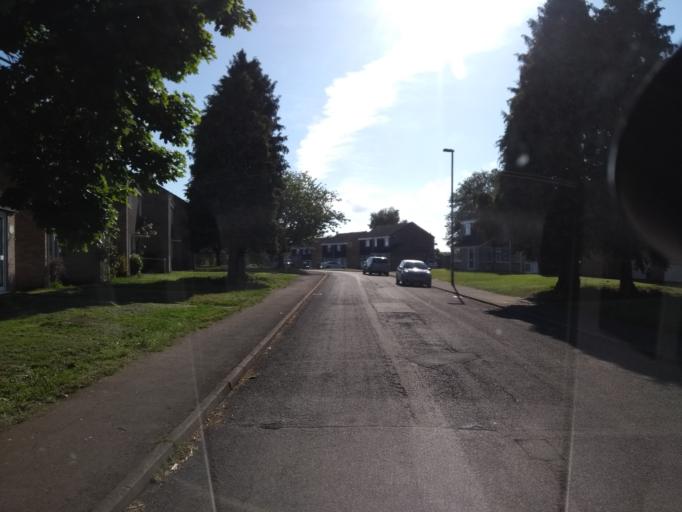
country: GB
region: England
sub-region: Somerset
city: Taunton
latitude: 51.0119
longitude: -3.0800
